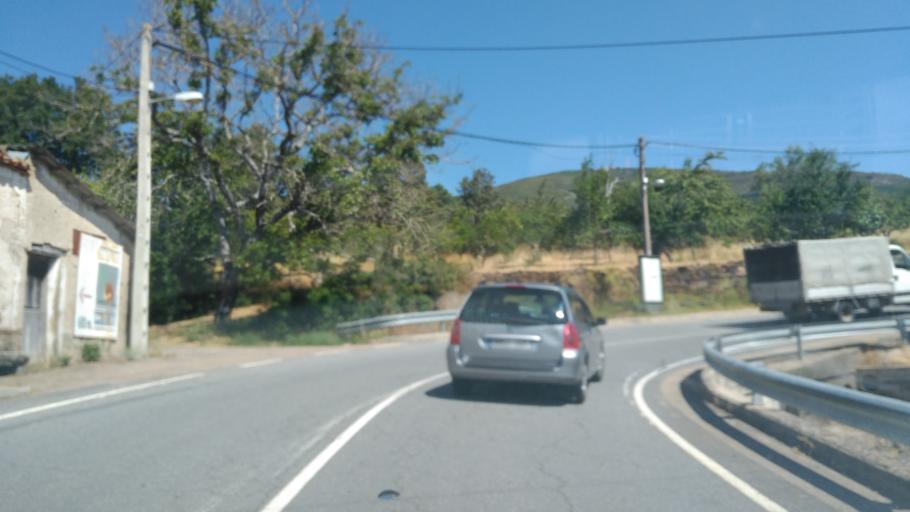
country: ES
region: Castille and Leon
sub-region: Provincia de Salamanca
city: San Martin del Castanar
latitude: 40.5374
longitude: -6.0473
